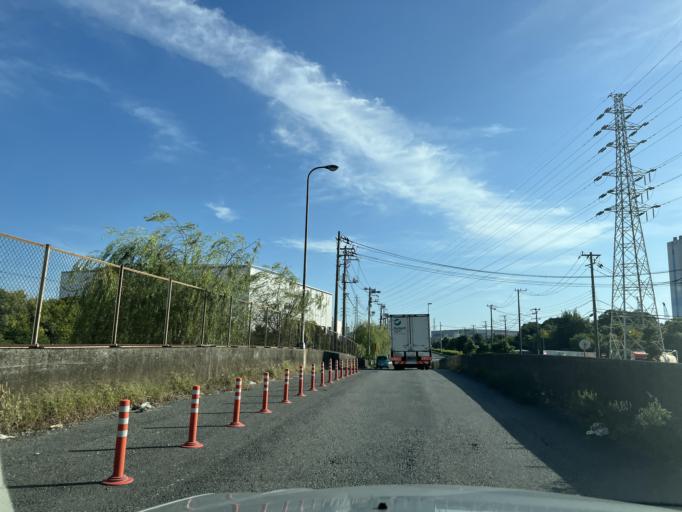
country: JP
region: Chiba
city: Funabashi
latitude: 35.6895
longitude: 139.9622
